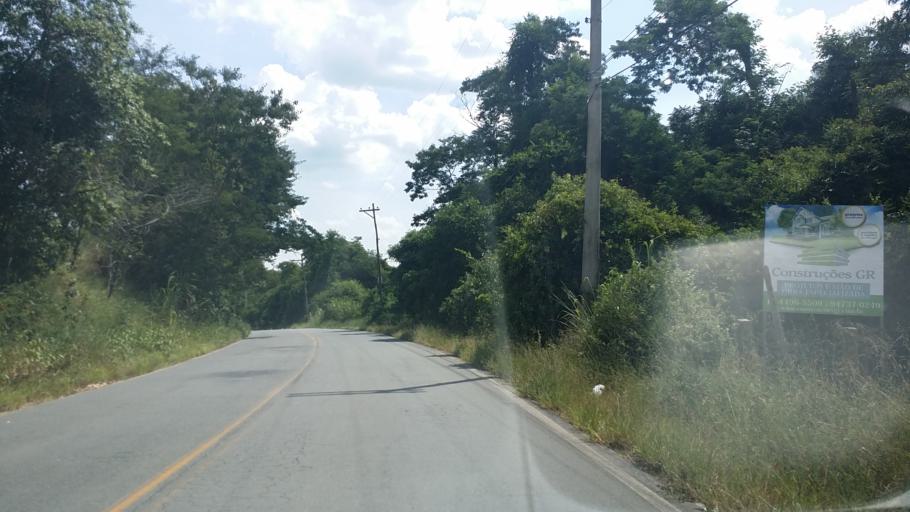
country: BR
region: Sao Paulo
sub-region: Itupeva
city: Itupeva
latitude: -23.1899
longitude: -47.0815
